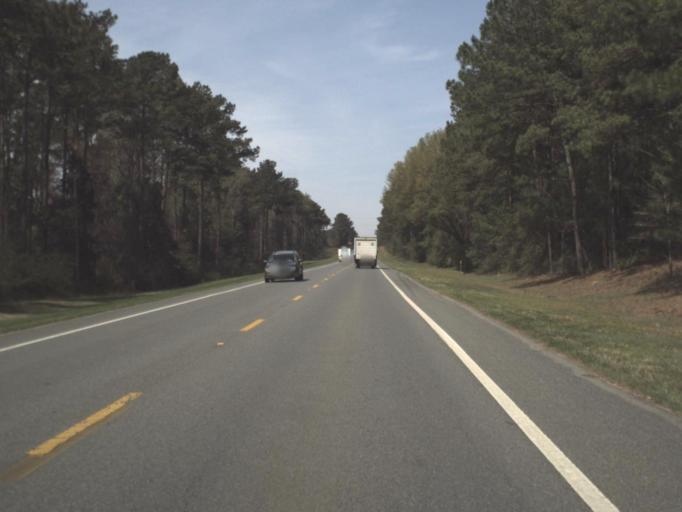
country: US
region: Florida
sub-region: Walton County
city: DeFuniak Springs
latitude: 30.7237
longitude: -85.9555
